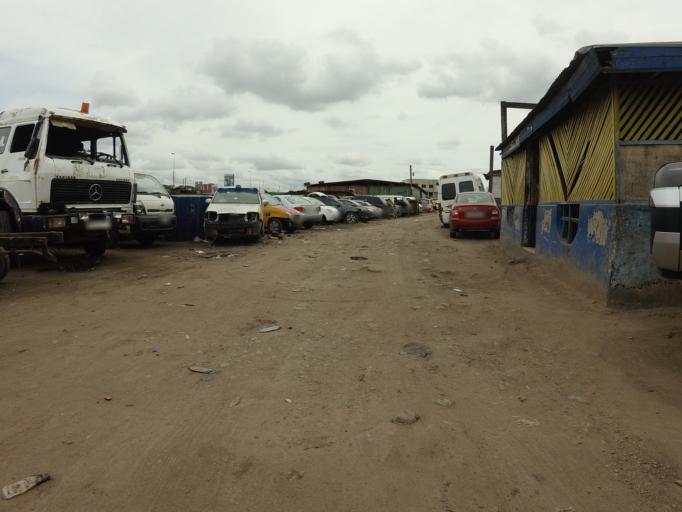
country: GH
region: Greater Accra
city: Accra
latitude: 5.5894
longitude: -0.2173
